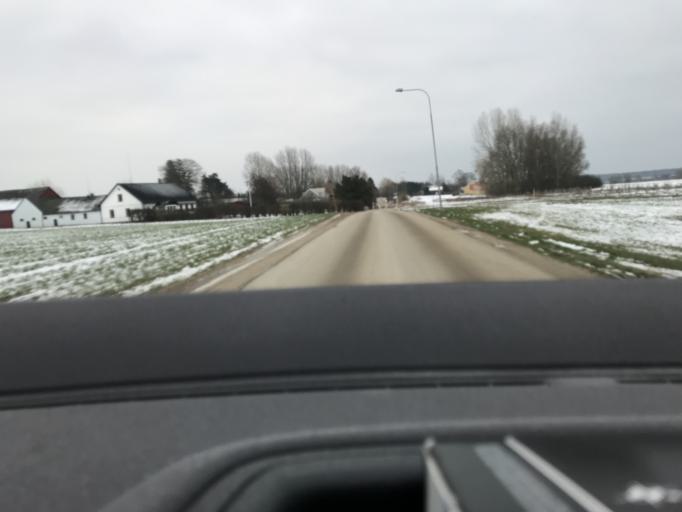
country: SE
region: Skane
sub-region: Ystads Kommun
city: Ystad
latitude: 55.4564
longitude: 13.8542
